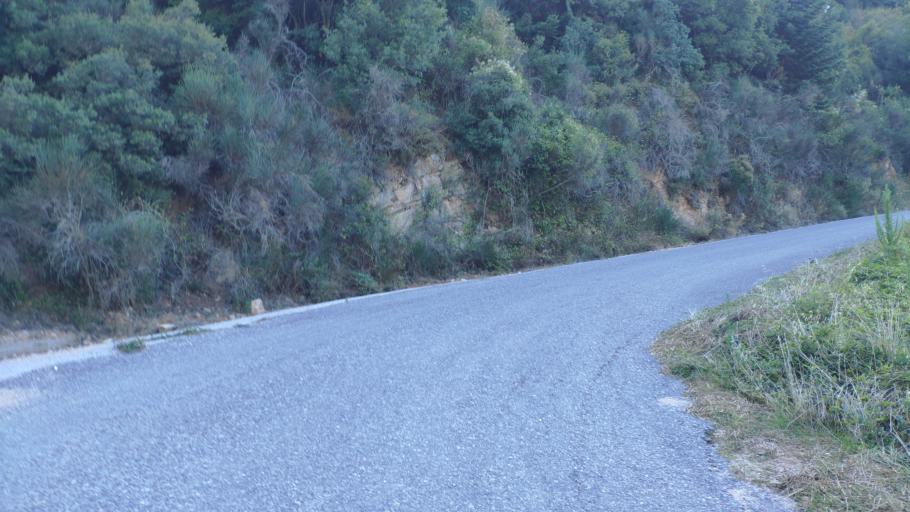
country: GR
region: Peloponnese
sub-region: Nomos Lakonias
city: Kariai
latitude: 37.1795
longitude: 22.5934
